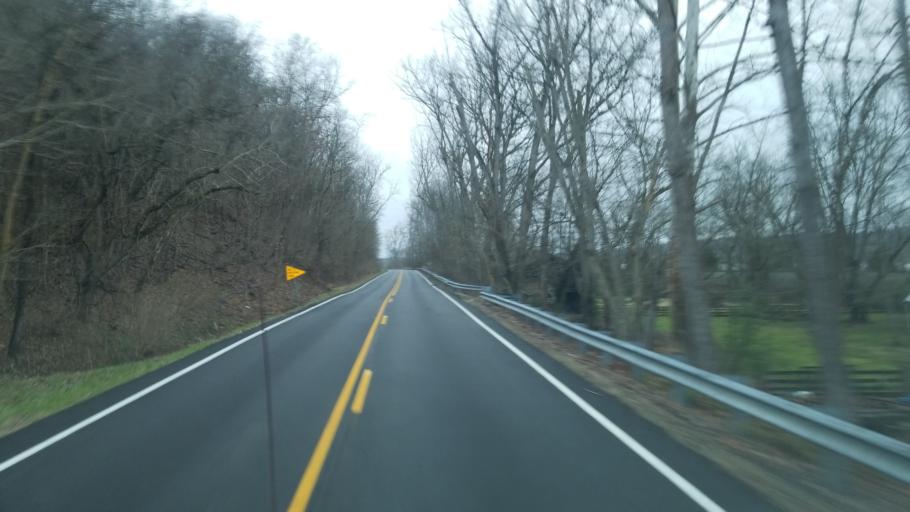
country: US
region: Kentucky
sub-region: Bracken County
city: Augusta
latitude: 38.7659
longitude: -84.0710
